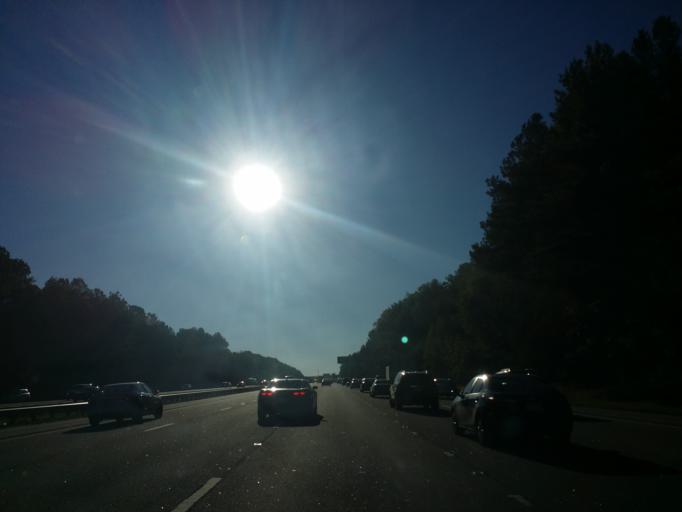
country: US
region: North Carolina
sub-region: Wake County
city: Cary
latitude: 35.8247
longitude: -78.7515
